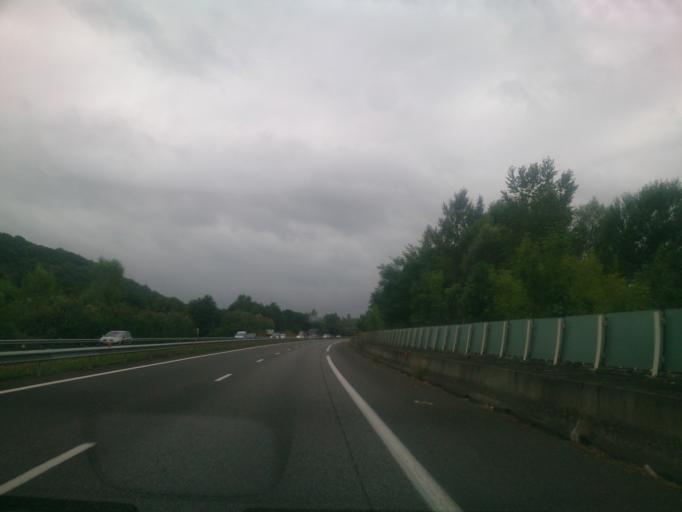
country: FR
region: Midi-Pyrenees
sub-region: Departement de la Haute-Garonne
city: Martres-Tolosane
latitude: 43.1766
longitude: 0.9780
